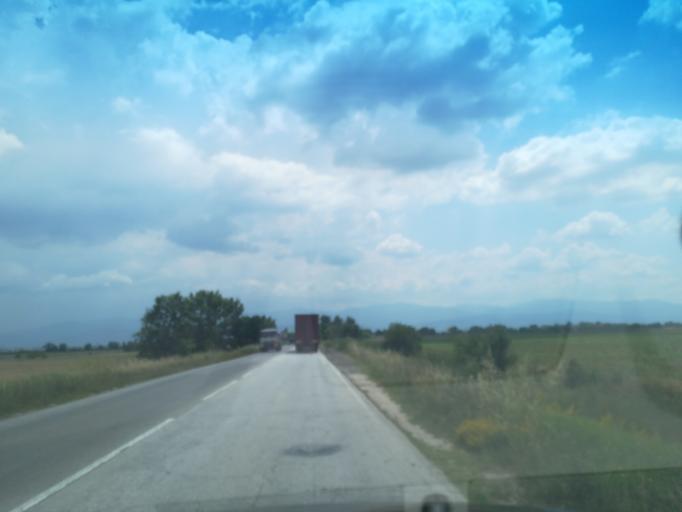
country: BG
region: Plovdiv
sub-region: Obshtina Plovdiv
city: Plovdiv
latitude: 42.1839
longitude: 24.6765
